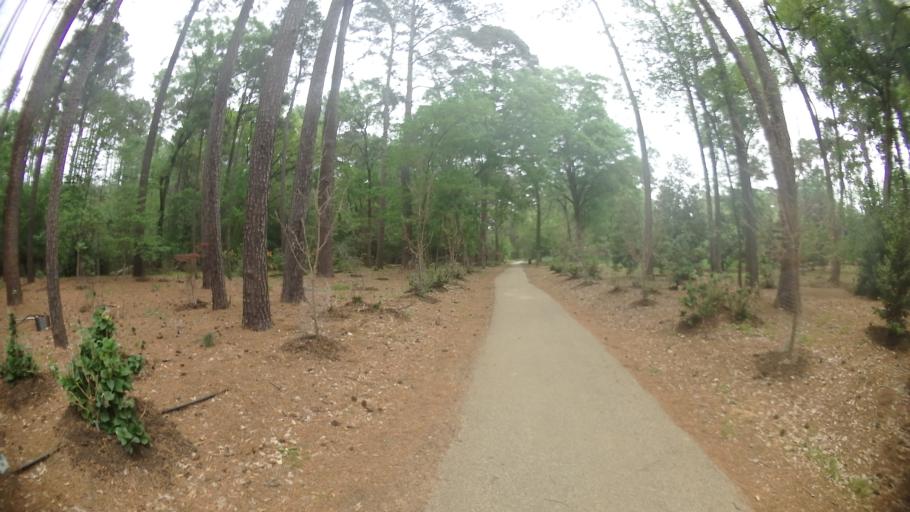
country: US
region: Texas
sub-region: Nacogdoches County
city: Nacogdoches
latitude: 31.6202
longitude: -94.6386
